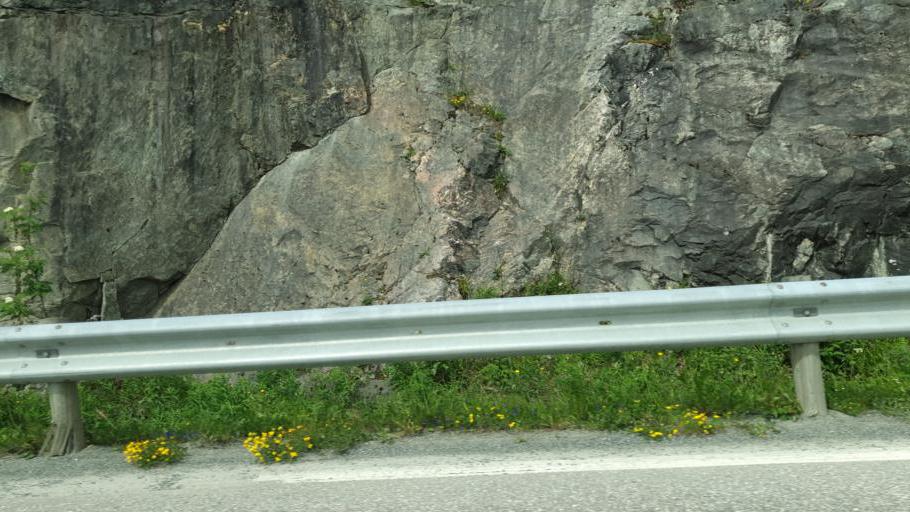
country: NO
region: Nord-Trondelag
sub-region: Leksvik
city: Leksvik
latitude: 63.6057
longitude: 10.4885
